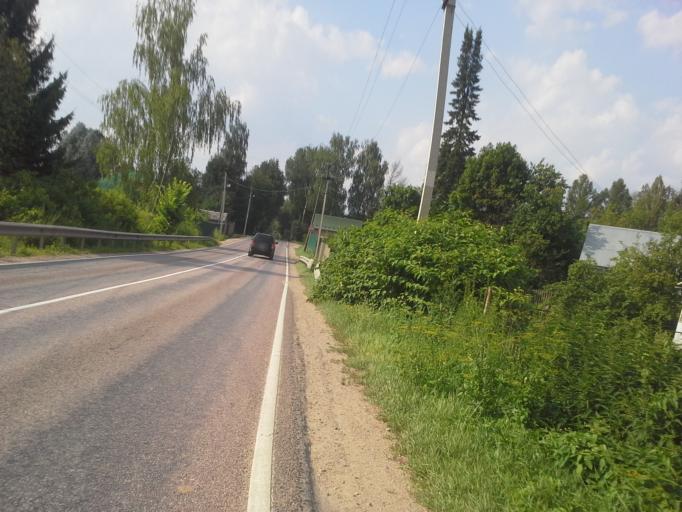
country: RU
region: Moskovskaya
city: Istra
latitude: 55.8905
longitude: 36.7962
